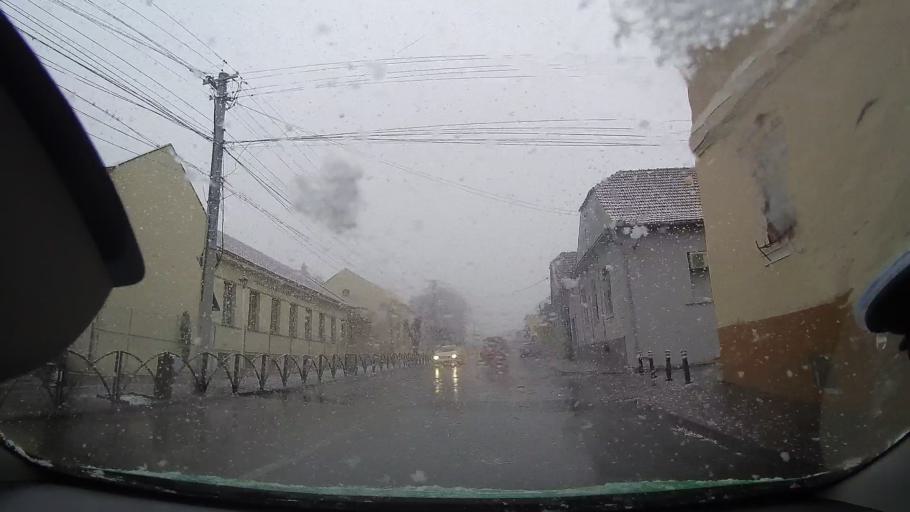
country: RO
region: Sibiu
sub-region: Municipiul Medias
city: Medias
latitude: 46.1692
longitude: 24.3514
